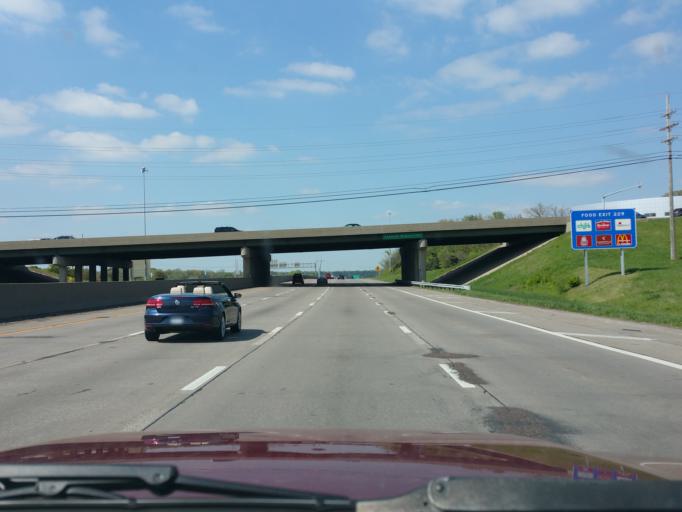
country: US
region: Kansas
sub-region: Johnson County
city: Merriam
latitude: 39.0137
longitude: -94.6930
